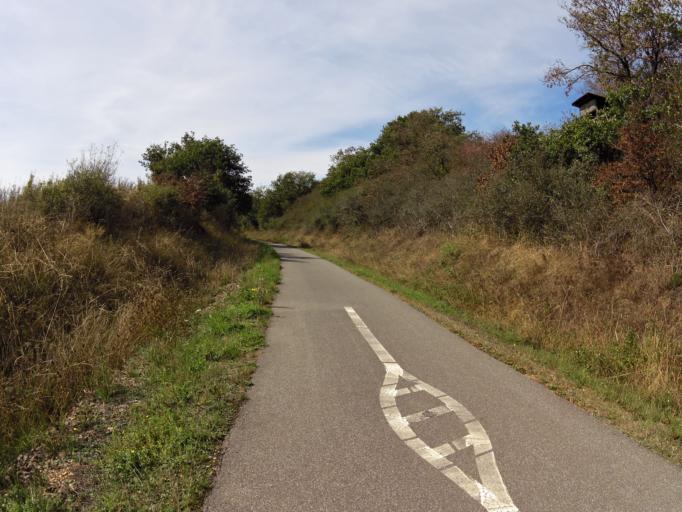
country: DE
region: Rheinland-Pfalz
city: Lichtenborn
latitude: 50.1152
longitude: 6.2769
